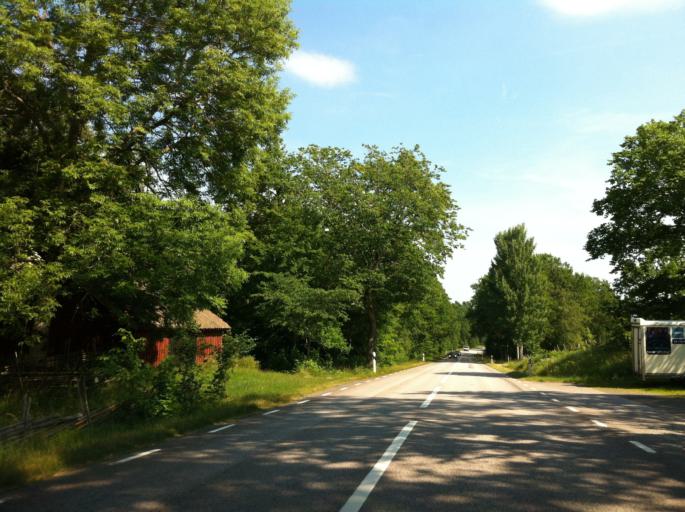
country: SE
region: Kalmar
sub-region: Nybro Kommun
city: Nybro
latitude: 56.7776
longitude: 15.8401
